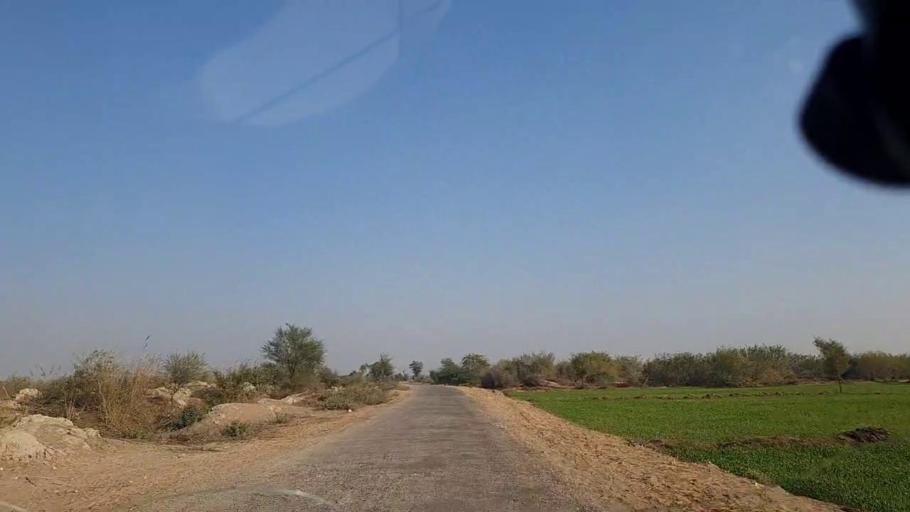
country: PK
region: Sindh
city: Khanpur
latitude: 27.6825
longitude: 69.5343
